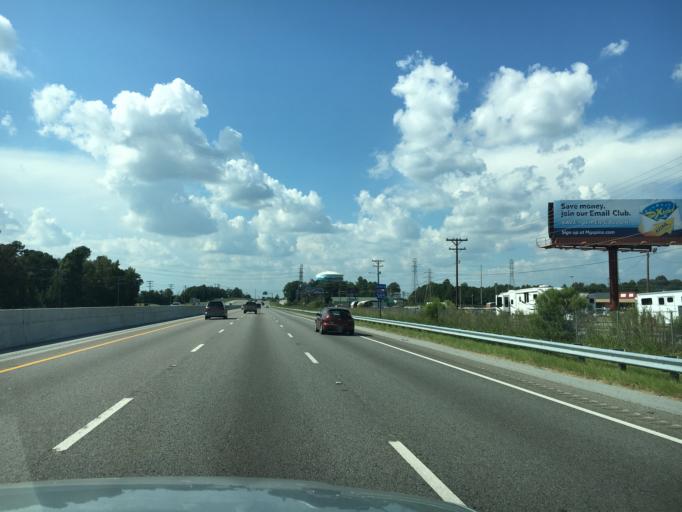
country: US
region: South Carolina
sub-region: Greenville County
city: Fountain Inn
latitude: 34.6908
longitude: -82.2220
